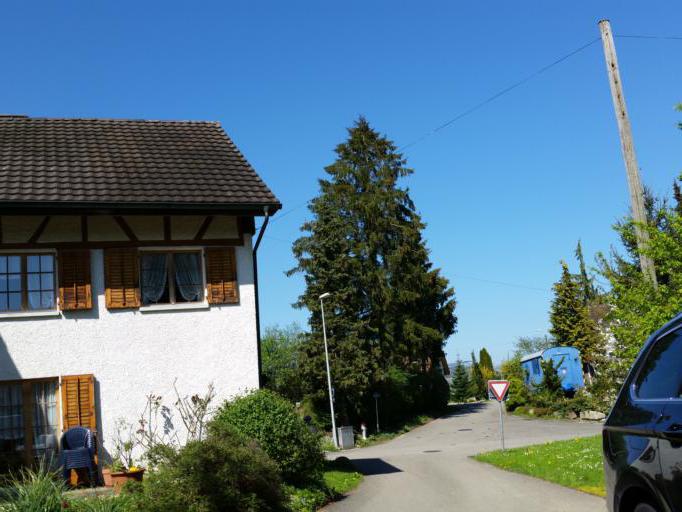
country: CH
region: Thurgau
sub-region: Arbon District
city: Salmsach
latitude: 47.5585
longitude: 9.3598
